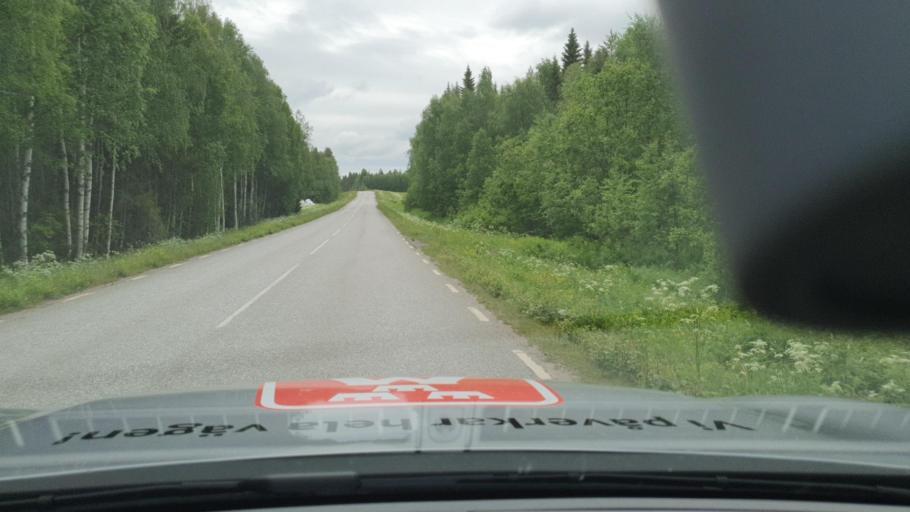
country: SE
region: Norrbotten
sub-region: Lulea Kommun
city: Ranea
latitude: 65.8935
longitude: 22.1865
